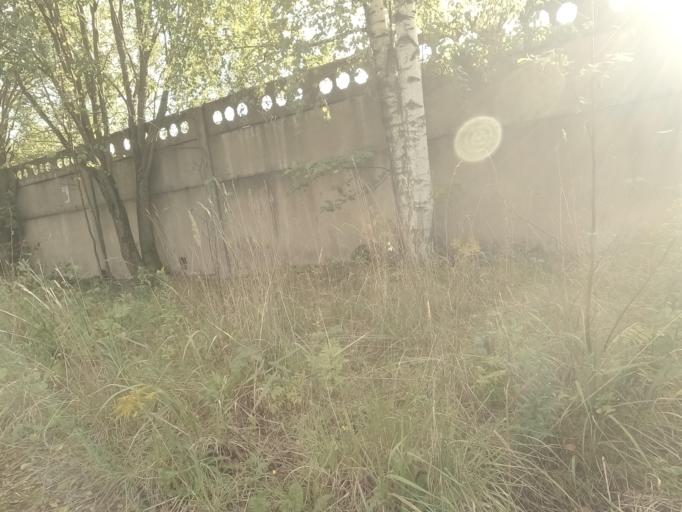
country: RU
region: St.-Petersburg
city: Krasnogvargeisky
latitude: 59.9753
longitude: 30.4873
